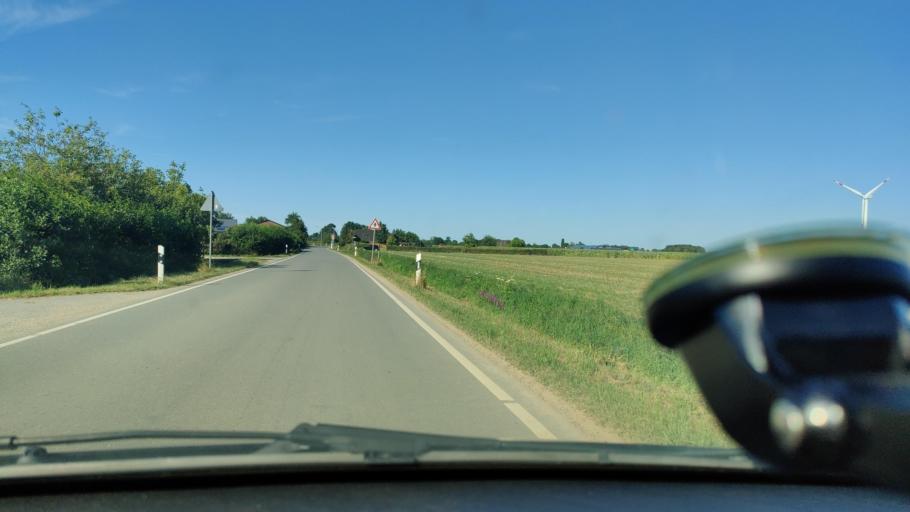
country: DE
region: North Rhine-Westphalia
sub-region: Regierungsbezirk Dusseldorf
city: Emmerich
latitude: 51.7738
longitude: 6.2133
